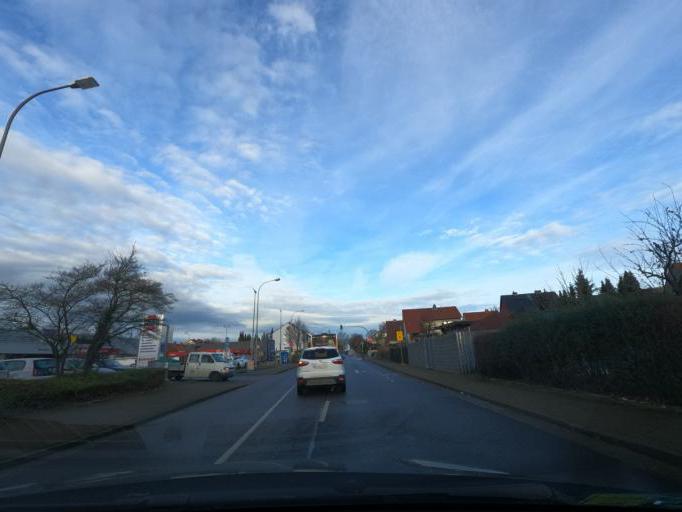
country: DE
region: Lower Saxony
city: Wolfenbuettel
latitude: 52.1510
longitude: 10.5560
